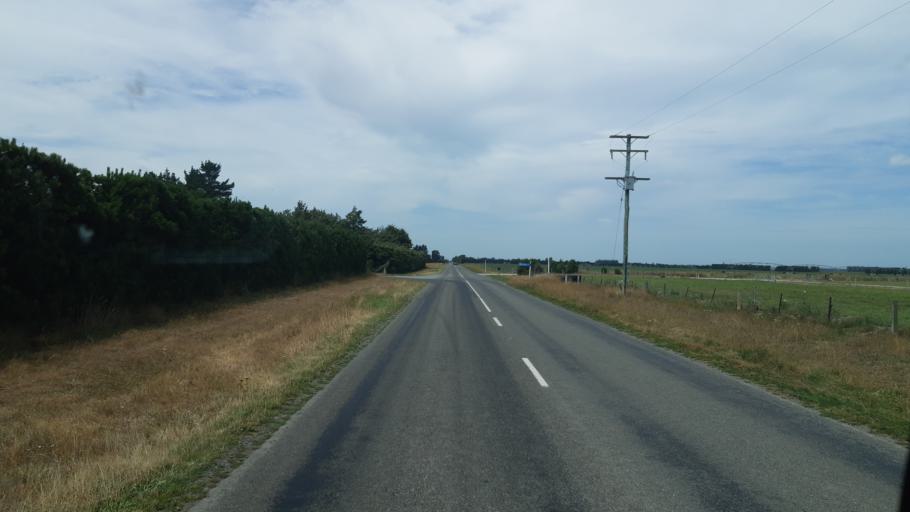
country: NZ
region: Canterbury
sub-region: Ashburton District
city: Tinwald
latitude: -43.9278
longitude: 171.5819
